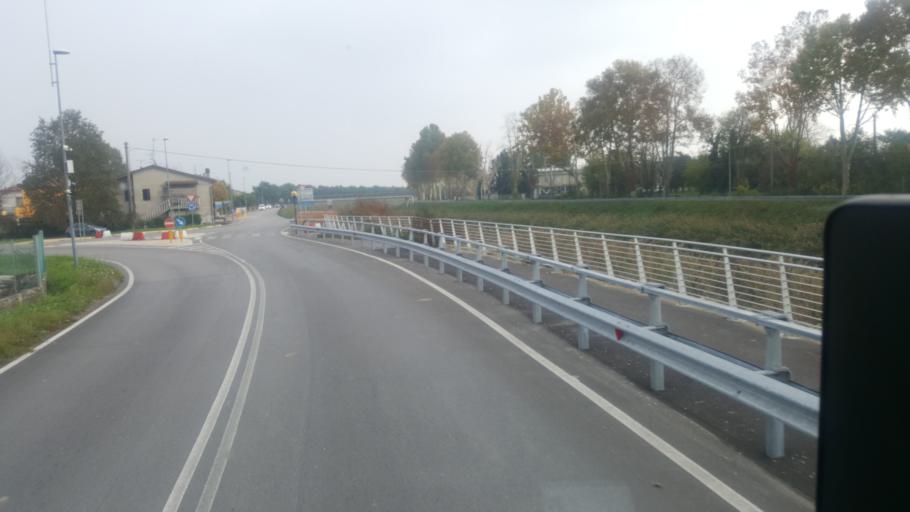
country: IT
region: Emilia-Romagna
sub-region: Provincia di Ferrara
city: Bondeno
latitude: 44.8951
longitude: 11.4036
